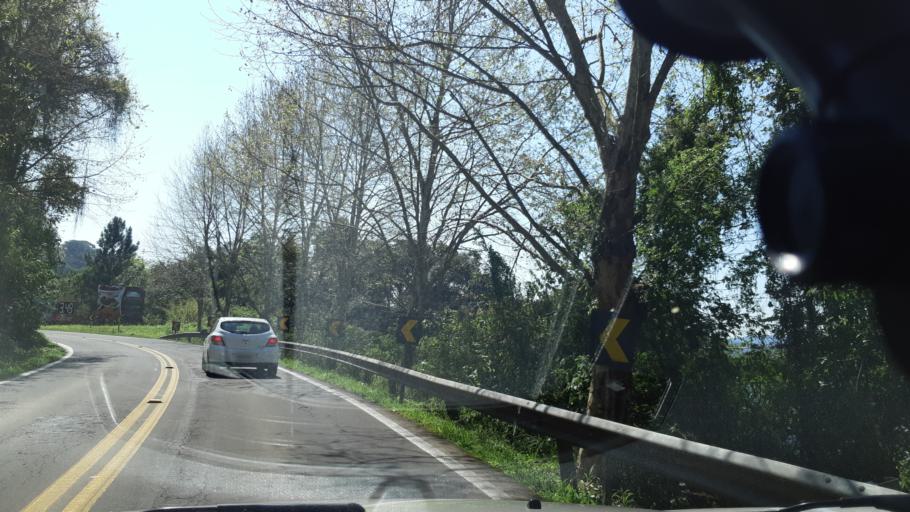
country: BR
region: Rio Grande do Sul
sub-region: Nova Petropolis
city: Nova Petropolis
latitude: -29.3943
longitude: -51.1234
